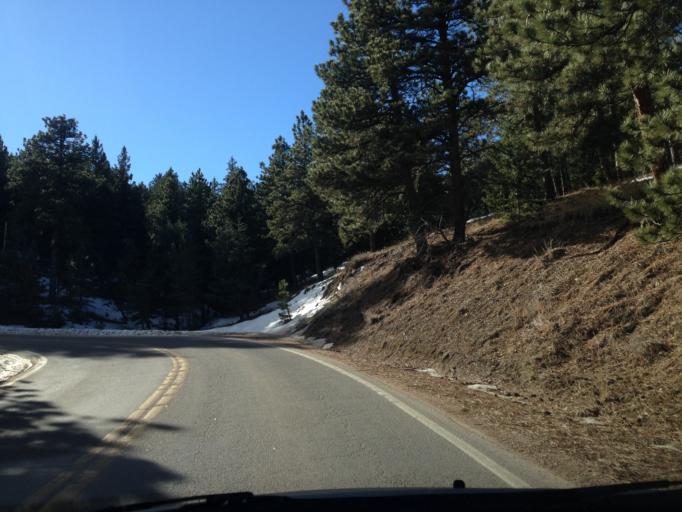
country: US
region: Colorado
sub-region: Boulder County
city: Boulder
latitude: 39.9959
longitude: -105.3114
